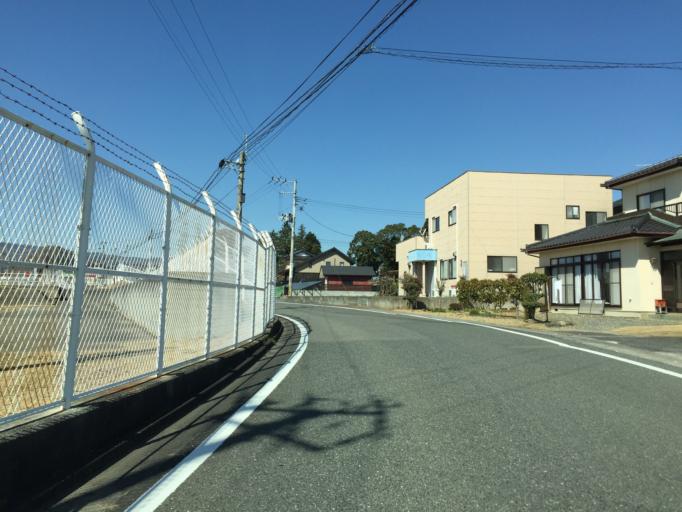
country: JP
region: Fukushima
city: Iwaki
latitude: 37.0606
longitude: 140.8492
